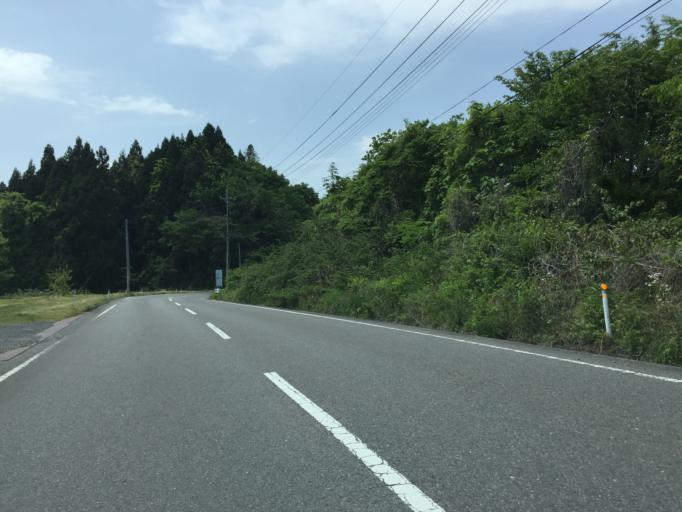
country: JP
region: Fukushima
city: Ishikawa
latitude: 37.1922
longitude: 140.4834
